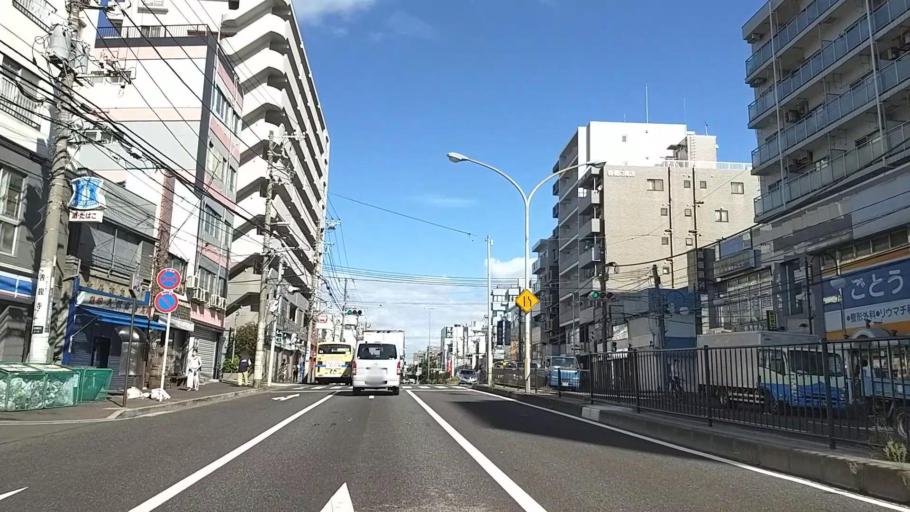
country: JP
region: Kanagawa
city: Yokohama
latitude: 35.4853
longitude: 139.6271
